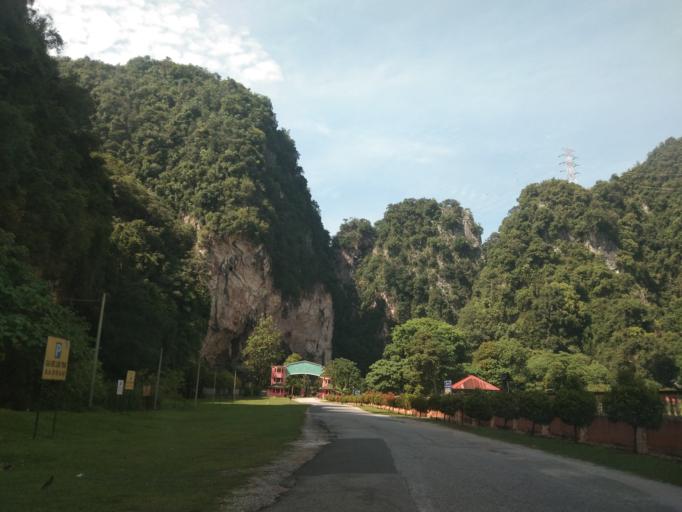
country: MY
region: Perak
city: Ipoh
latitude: 4.5607
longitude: 101.1295
